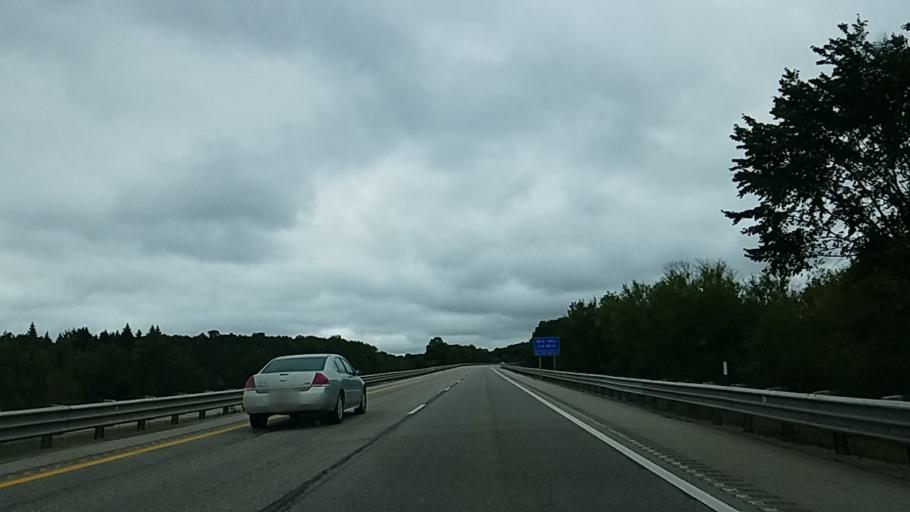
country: US
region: Michigan
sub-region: Otsego County
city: Gaylord
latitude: 45.1282
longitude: -84.6720
